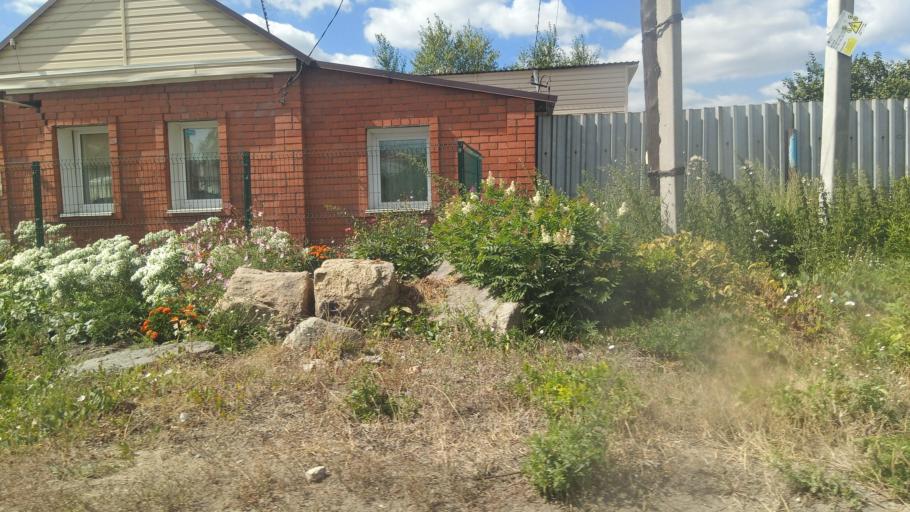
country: RU
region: Chelyabinsk
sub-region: Gorod Chelyabinsk
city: Chelyabinsk
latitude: 55.1255
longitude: 61.3917
